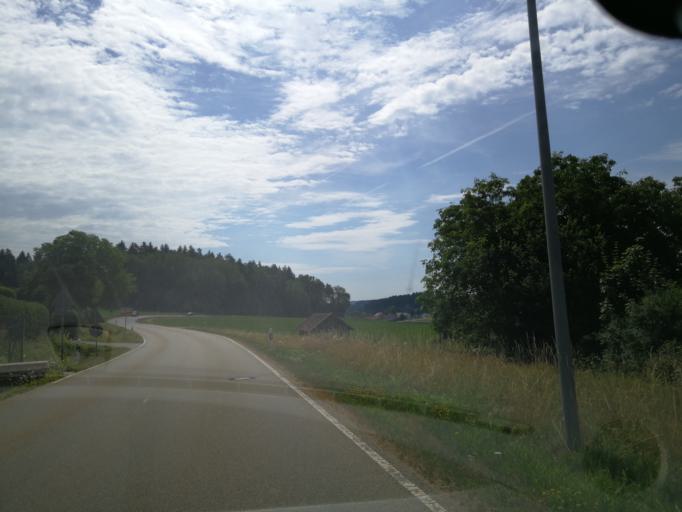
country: DE
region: Bavaria
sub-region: Upper Palatinate
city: Falkenstein
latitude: 49.0891
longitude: 12.5014
